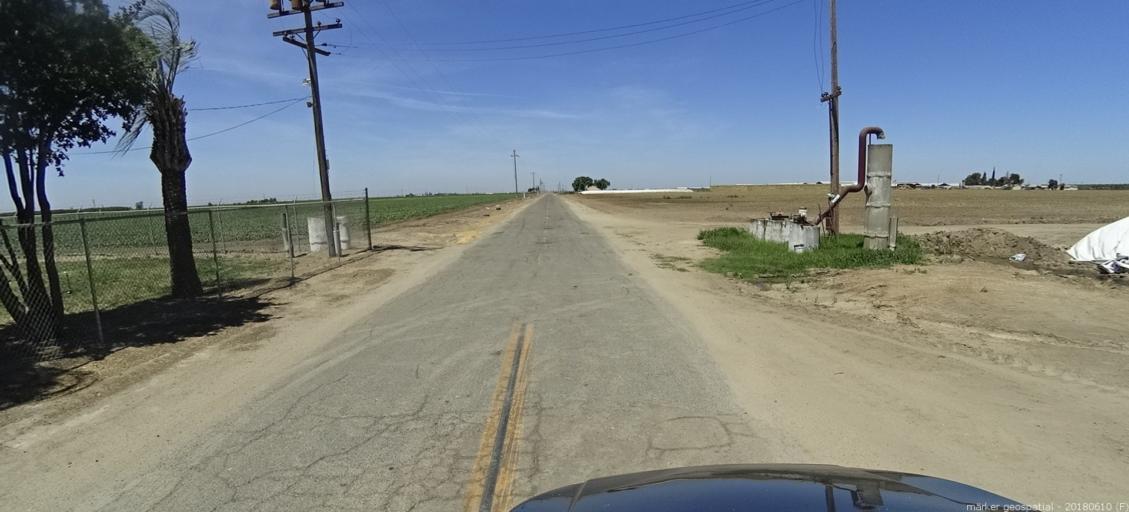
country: US
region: California
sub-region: Madera County
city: Chowchilla
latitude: 37.0546
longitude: -120.4377
